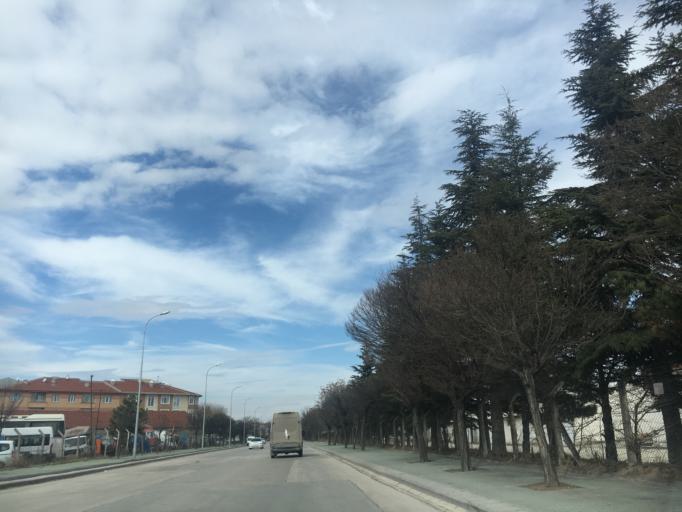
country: TR
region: Eskisehir
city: Eskisehir
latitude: 39.7785
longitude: 30.5350
